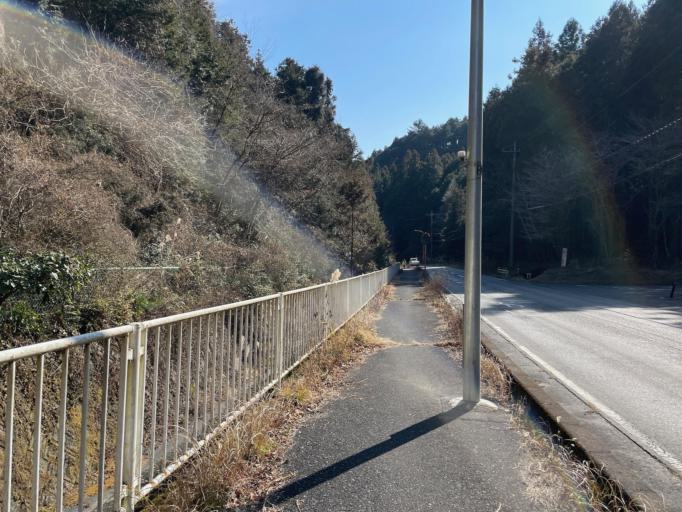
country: JP
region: Saitama
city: Hanno
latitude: 35.8536
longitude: 139.2489
